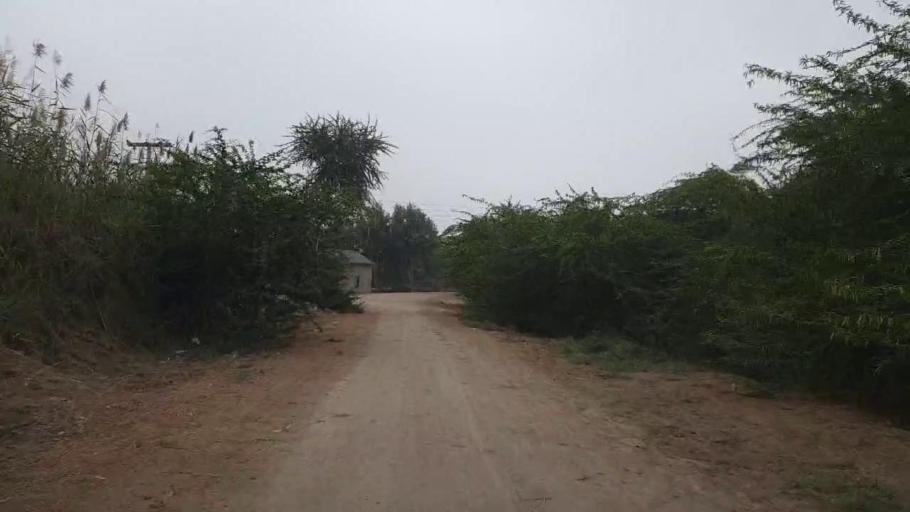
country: PK
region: Sindh
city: Badin
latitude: 24.5964
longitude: 68.6766
